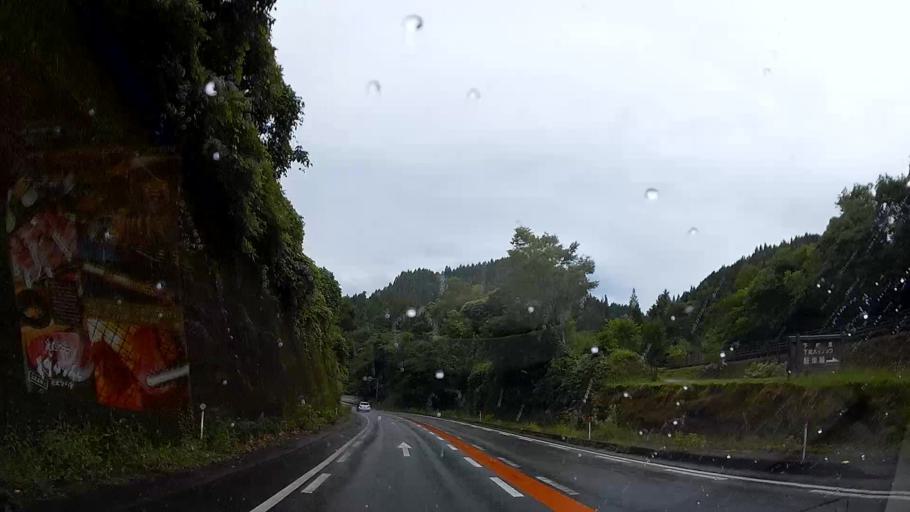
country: JP
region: Oita
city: Tsukawaki
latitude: 33.1509
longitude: 131.0535
